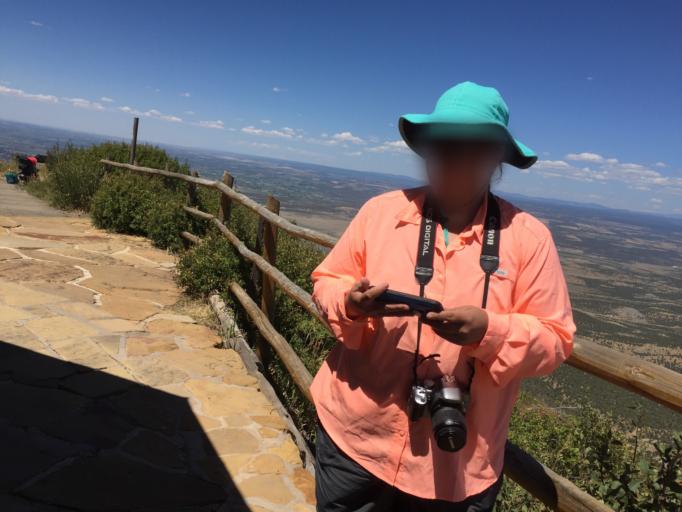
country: US
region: Colorado
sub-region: Montezuma County
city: Cortez
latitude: 37.2807
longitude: -108.4615
